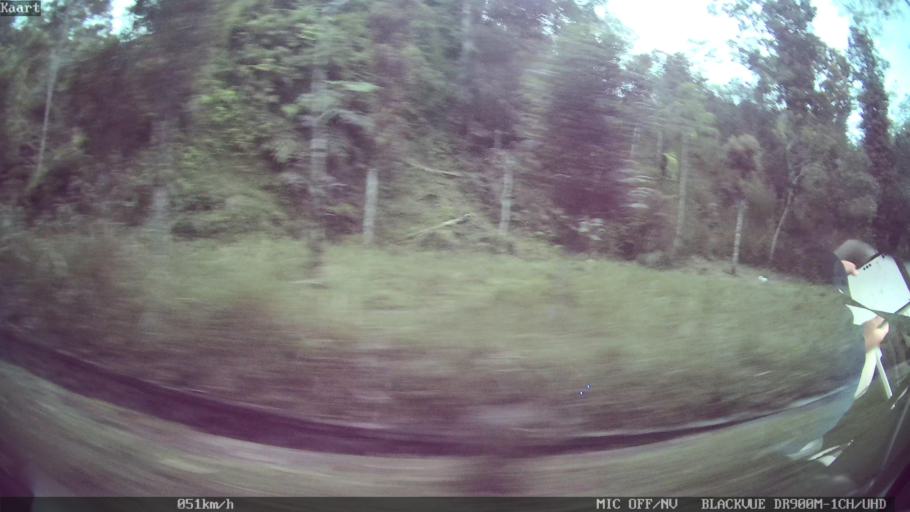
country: ID
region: Bali
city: Banjar Bias
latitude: -8.3754
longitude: 115.4423
